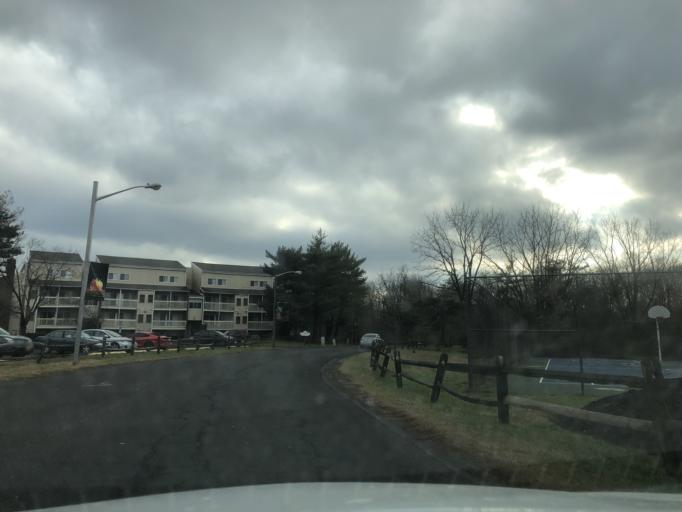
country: US
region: New Jersey
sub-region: Camden County
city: Glendora
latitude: 39.8267
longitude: -75.0790
